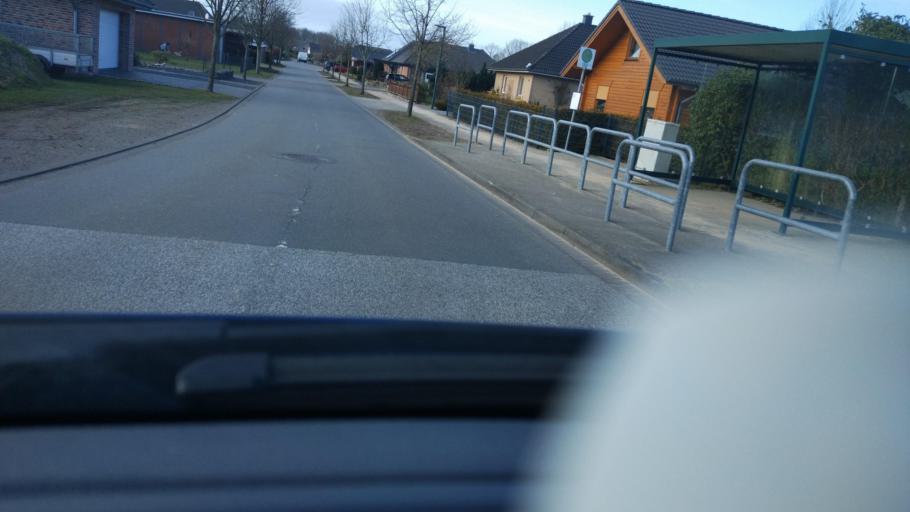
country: DE
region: Schleswig-Holstein
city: Silberstedt
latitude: 54.5177
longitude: 9.3641
